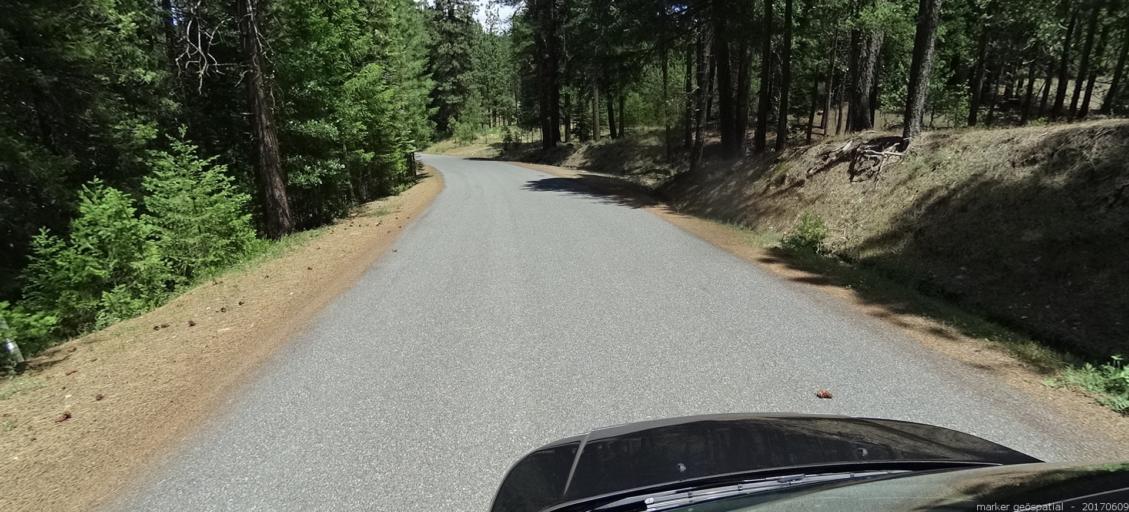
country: US
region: California
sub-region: Siskiyou County
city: Yreka
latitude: 41.3631
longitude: -122.9000
